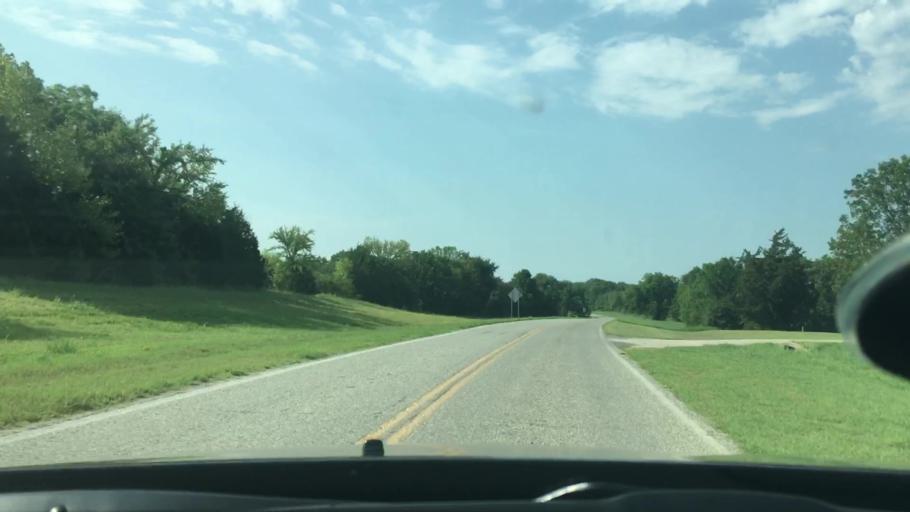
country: US
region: Oklahoma
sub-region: Johnston County
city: Tishomingo
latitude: 34.2285
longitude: -96.6350
